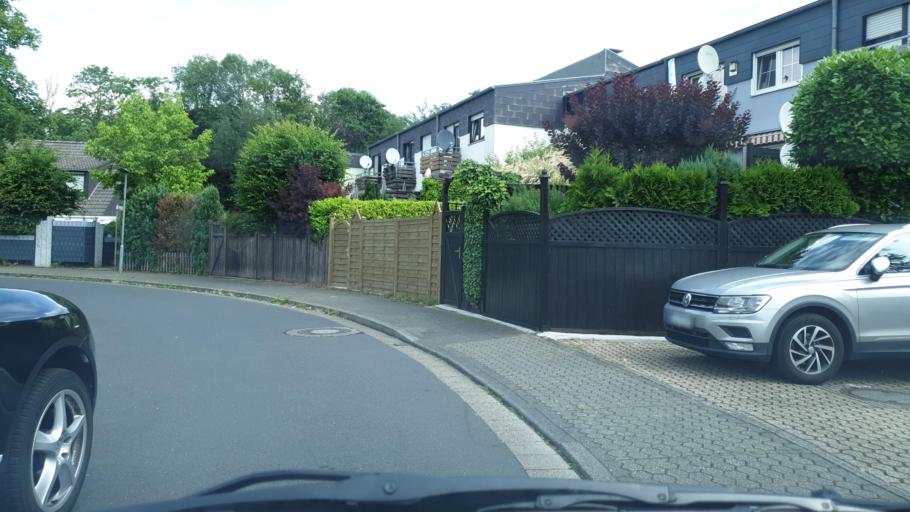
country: DE
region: North Rhine-Westphalia
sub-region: Regierungsbezirk Koln
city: Kerpen
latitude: 50.9229
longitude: 6.7058
